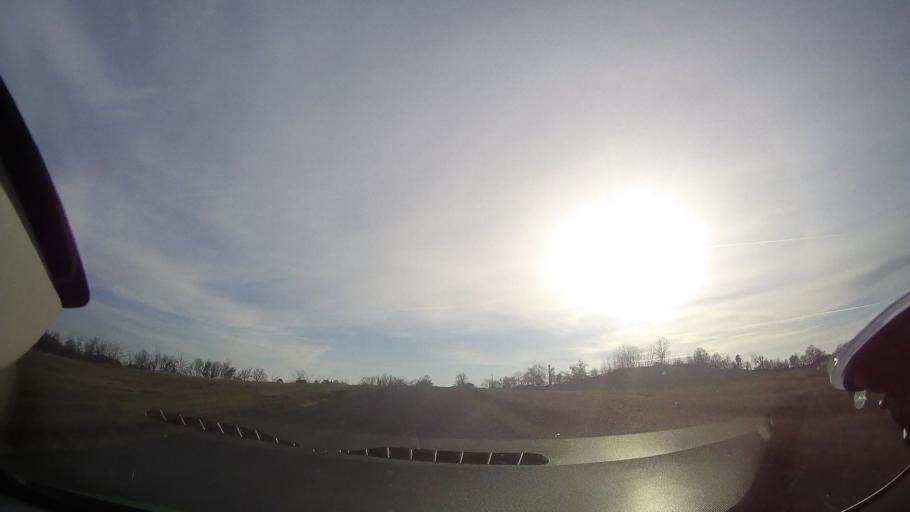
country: RO
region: Bihor
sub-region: Comuna Sarbi
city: Burzuc
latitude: 47.1259
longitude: 22.1859
